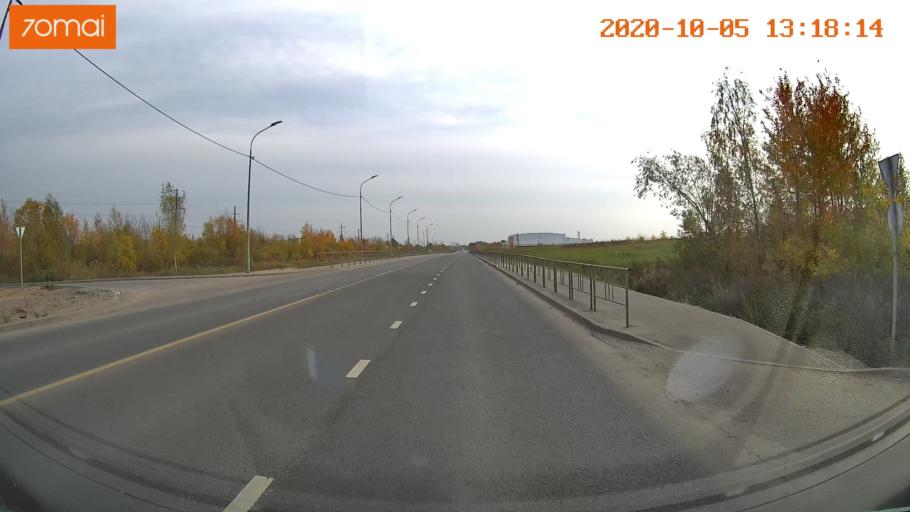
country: RU
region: Ivanovo
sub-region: Gorod Ivanovo
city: Ivanovo
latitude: 56.9791
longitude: 40.9180
